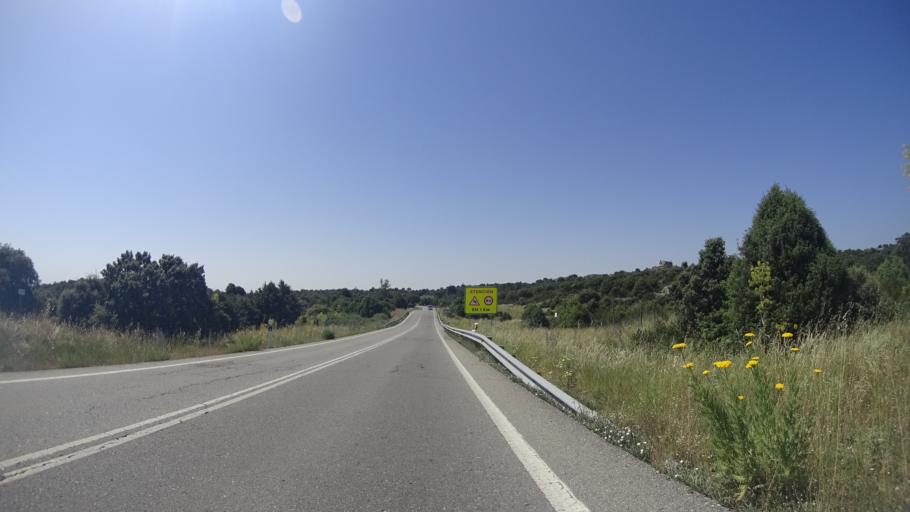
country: ES
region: Madrid
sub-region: Provincia de Madrid
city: Torrelodones
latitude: 40.5969
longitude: -3.9191
